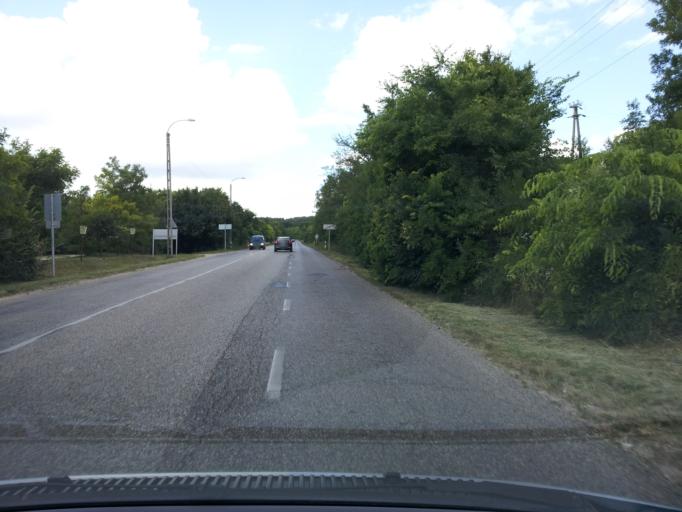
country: HU
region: Veszprem
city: Balatonalmadi
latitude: 47.0512
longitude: 18.0029
